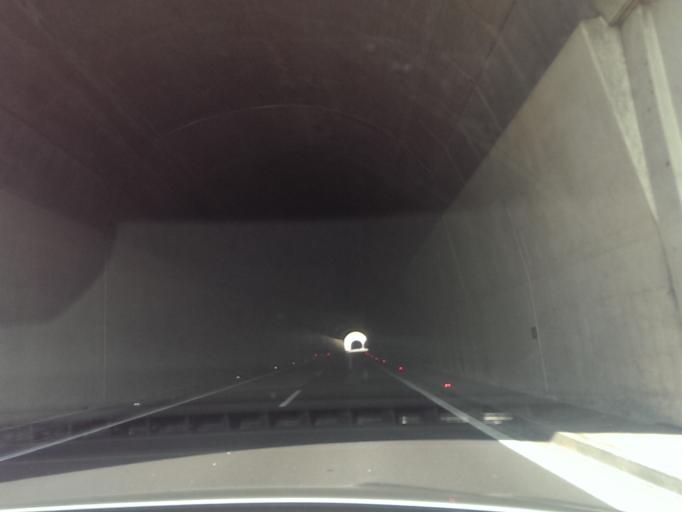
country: AT
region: Upper Austria
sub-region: Politischer Bezirk Kirchdorf an der Krems
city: Kremsmunster
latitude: 47.9730
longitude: 14.0936
